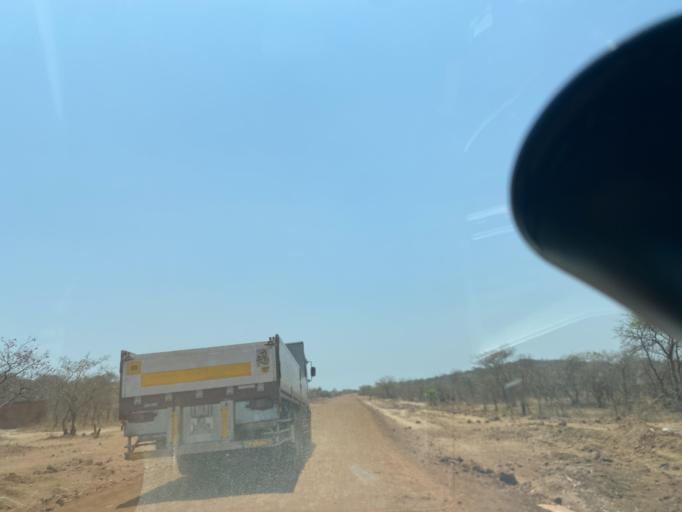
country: ZM
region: Lusaka
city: Lusaka
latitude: -15.4487
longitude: 27.9549
